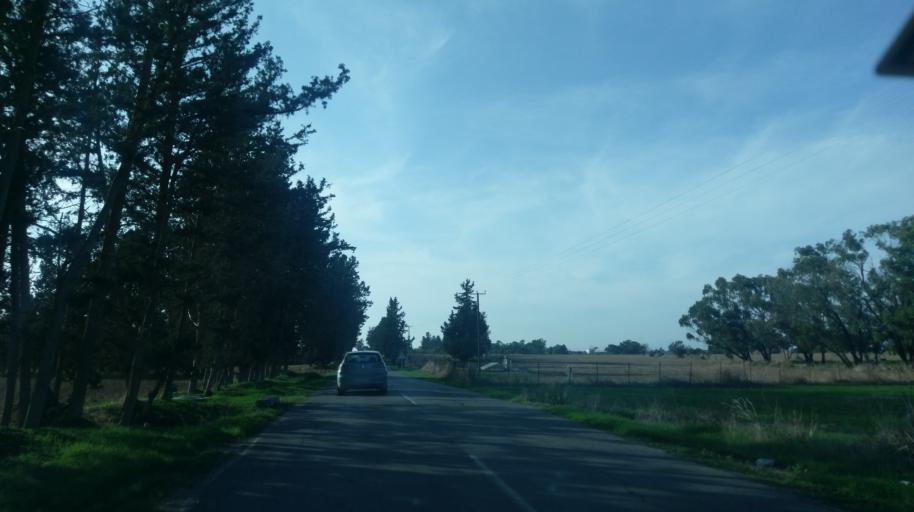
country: CY
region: Ammochostos
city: Achna
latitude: 35.1098
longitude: 33.7403
